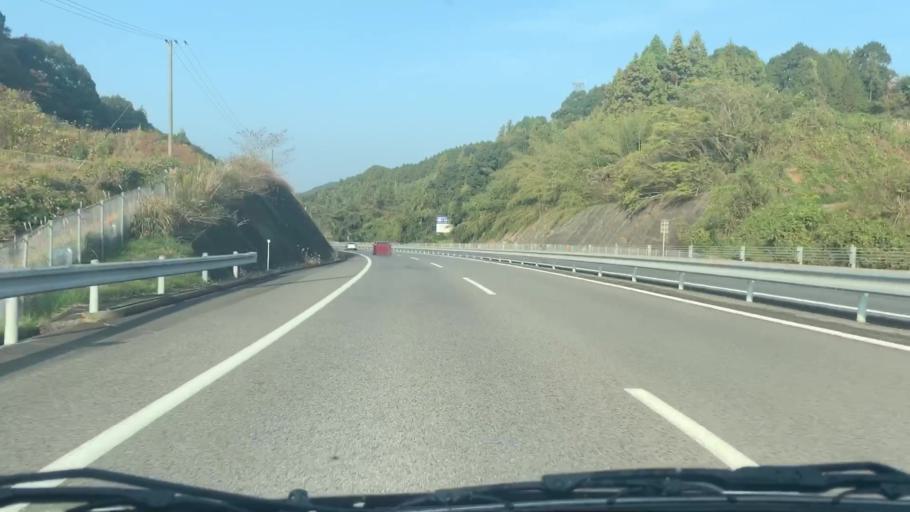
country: JP
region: Saga Prefecture
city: Ureshinomachi-shimojuku
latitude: 33.1541
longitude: 129.9318
